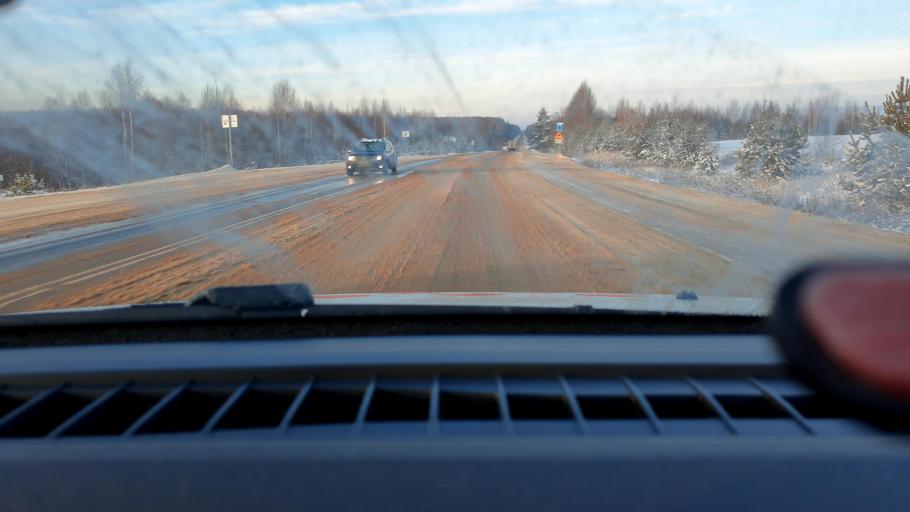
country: RU
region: Nizjnij Novgorod
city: Sharanga
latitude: 57.2159
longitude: 46.5055
